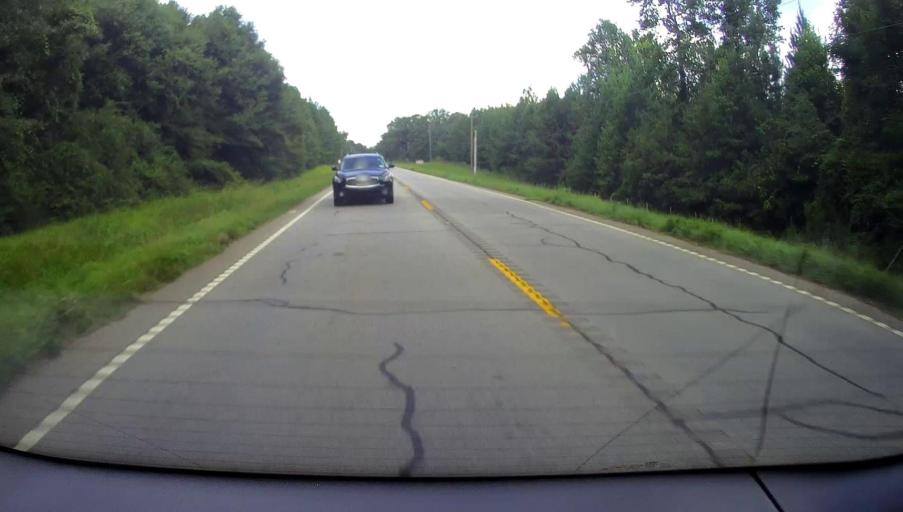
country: US
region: Georgia
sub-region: Meriwether County
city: Greenville
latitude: 33.1048
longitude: -84.5862
